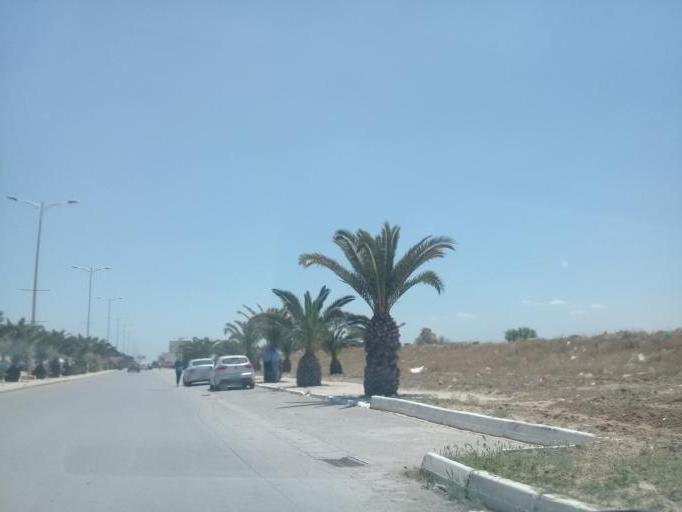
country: TN
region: Tunis
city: La Goulette
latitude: 36.8453
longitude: 10.2605
